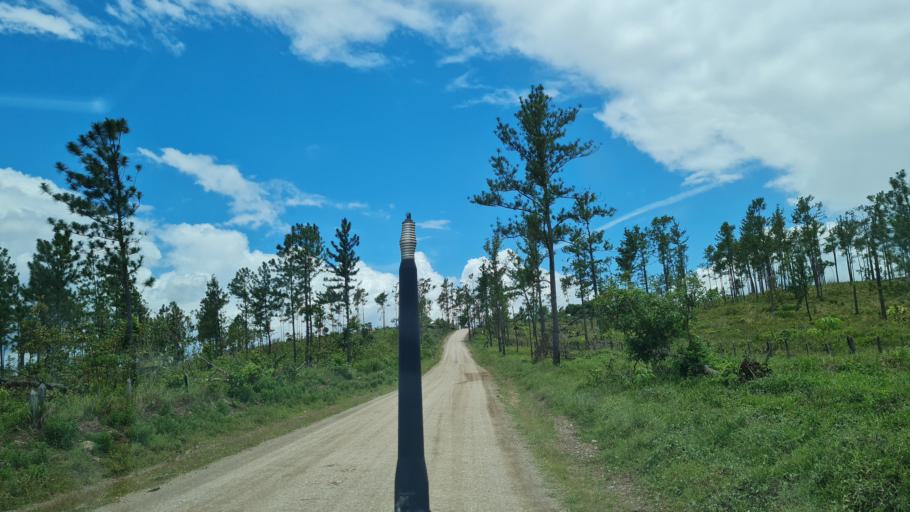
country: NI
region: Atlantico Norte (RAAN)
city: Siuna
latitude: 13.5753
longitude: -84.3236
